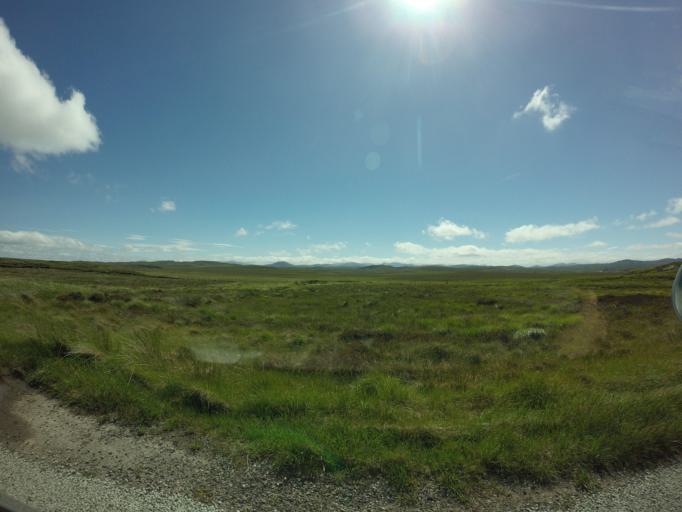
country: GB
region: Scotland
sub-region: Eilean Siar
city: Isle of Lewis
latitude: 58.1866
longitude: -6.6852
